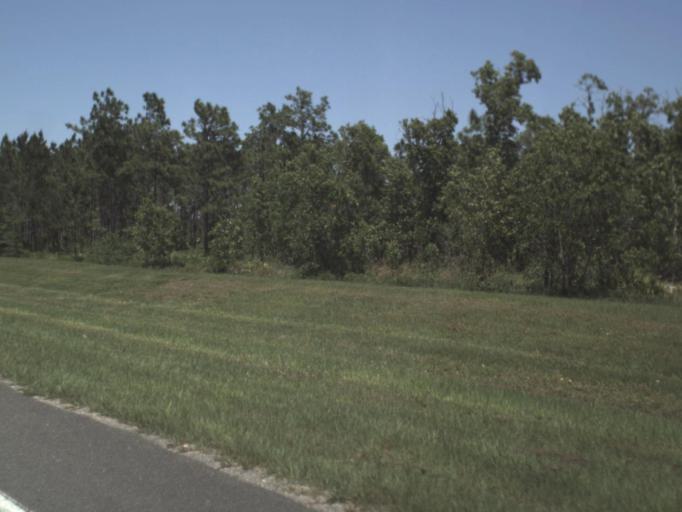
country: US
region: Florida
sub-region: Clay County
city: Lakeside
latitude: 30.1689
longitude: -81.8313
